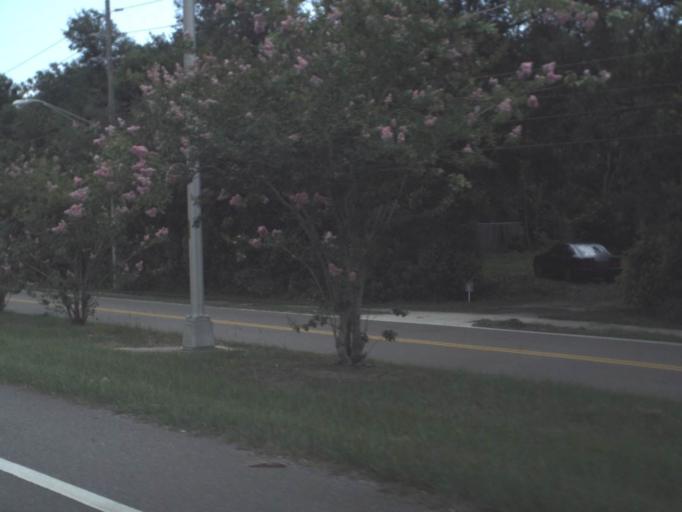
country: US
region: Florida
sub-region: Duval County
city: Jacksonville
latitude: 30.3077
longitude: -81.5586
